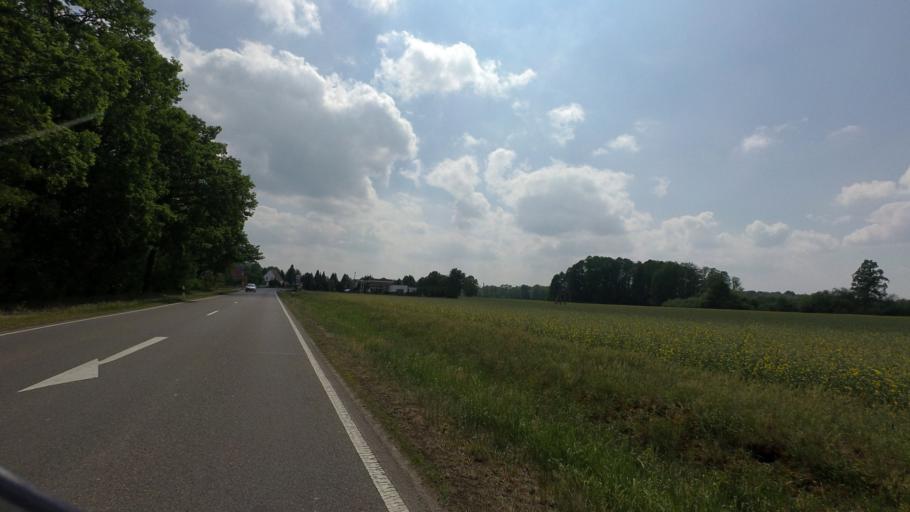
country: DE
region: Saxony
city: Rietschen
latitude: 51.4059
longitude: 14.7871
